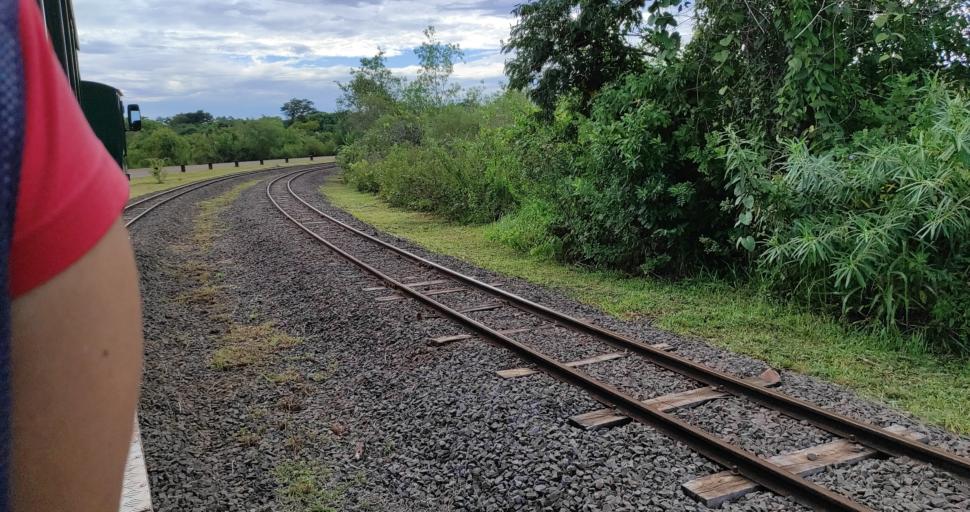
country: AR
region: Misiones
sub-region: Departamento de Iguazu
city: Puerto Iguazu
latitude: -25.6764
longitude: -54.4531
